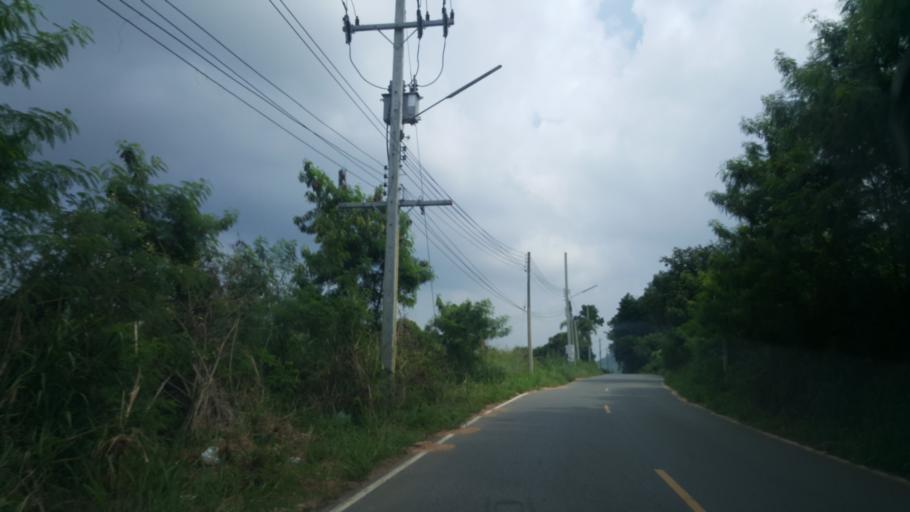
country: TH
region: Chon Buri
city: Sattahip
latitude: 12.7113
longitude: 100.9109
